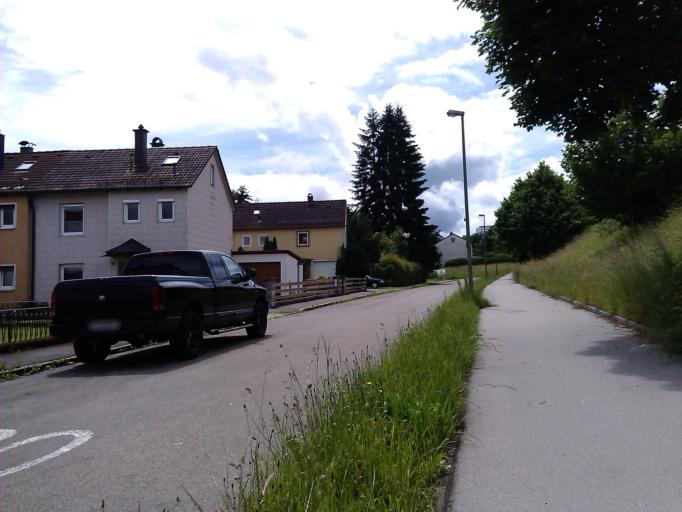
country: DE
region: Bavaria
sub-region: Swabia
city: Kaufbeuren
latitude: 47.8969
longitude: 10.6119
